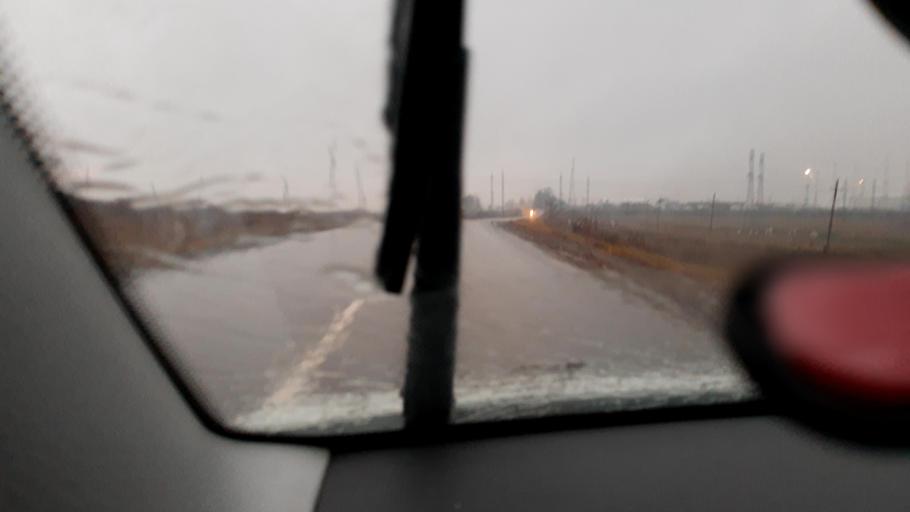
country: RU
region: Bashkortostan
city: Blagoveshchensk
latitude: 54.9010
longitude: 56.1778
